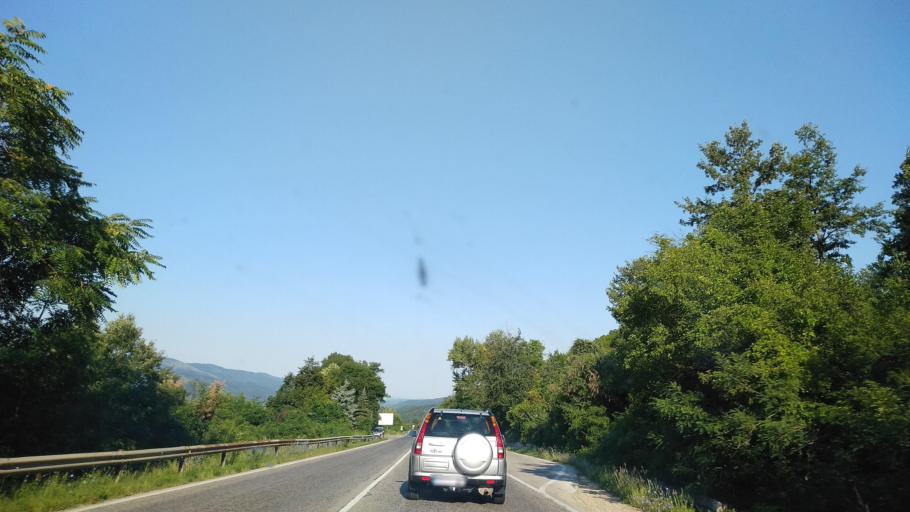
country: BG
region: Lovech
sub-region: Obshtina Lovech
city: Lovech
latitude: 43.0479
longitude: 24.7789
